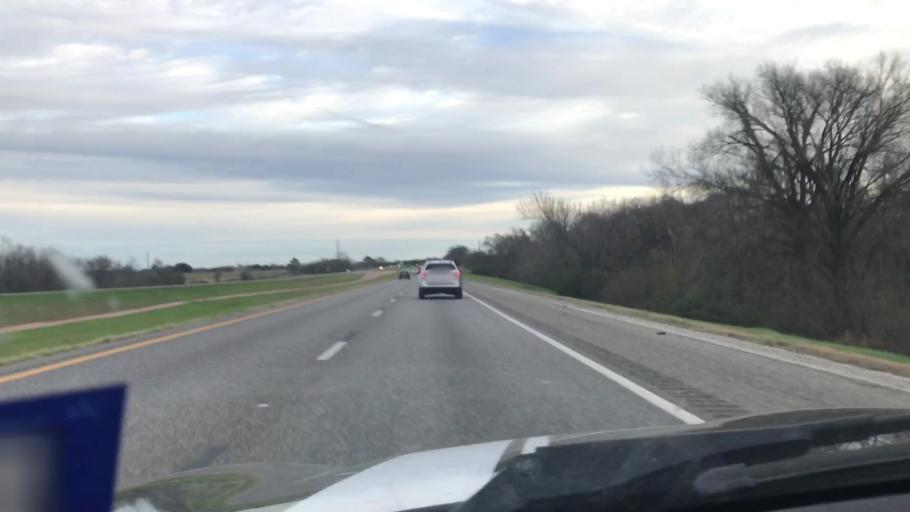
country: US
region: Texas
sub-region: Waller County
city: Hempstead
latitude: 30.1299
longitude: -96.1516
